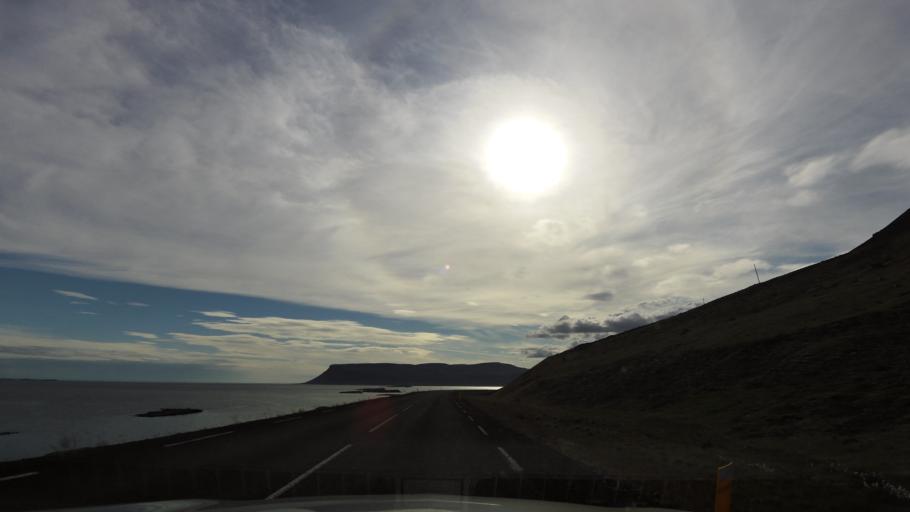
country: IS
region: Westfjords
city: Isafjoerdur
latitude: 65.5411
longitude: -23.0251
